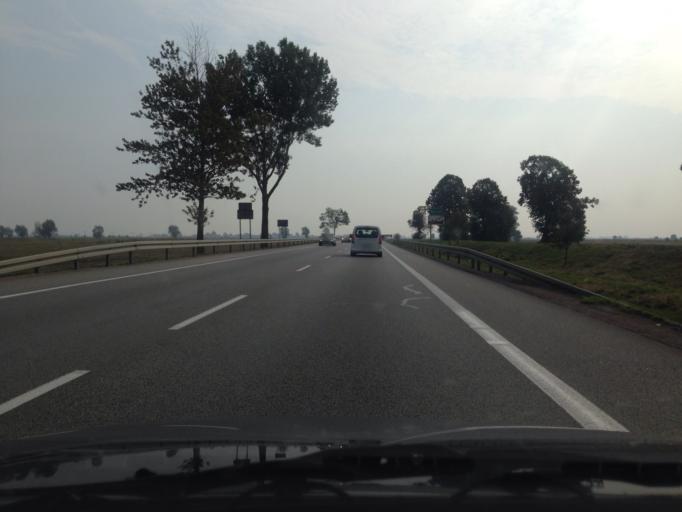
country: PL
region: Pomeranian Voivodeship
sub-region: Powiat nowodworski
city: Ostaszewo
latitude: 54.2477
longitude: 18.9850
